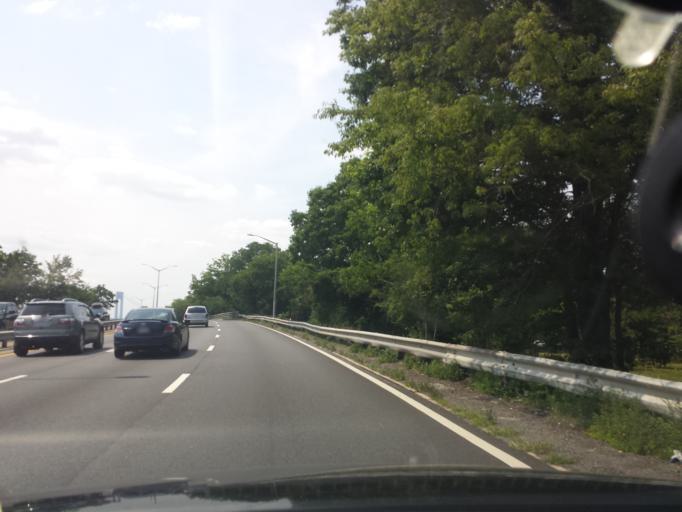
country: US
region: New York
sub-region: Kings County
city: Bensonhurst
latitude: 40.5954
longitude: -73.9987
